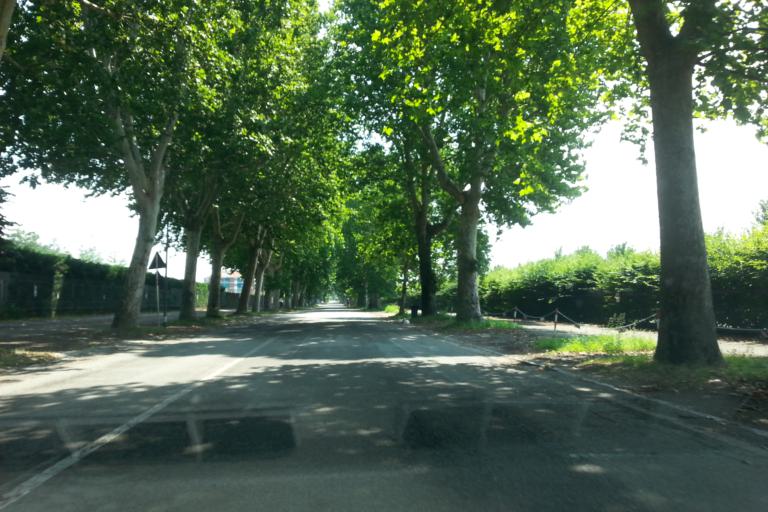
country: IT
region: Piedmont
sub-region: Provincia di Torino
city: Venaria Reale
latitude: 45.1395
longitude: 7.6184
